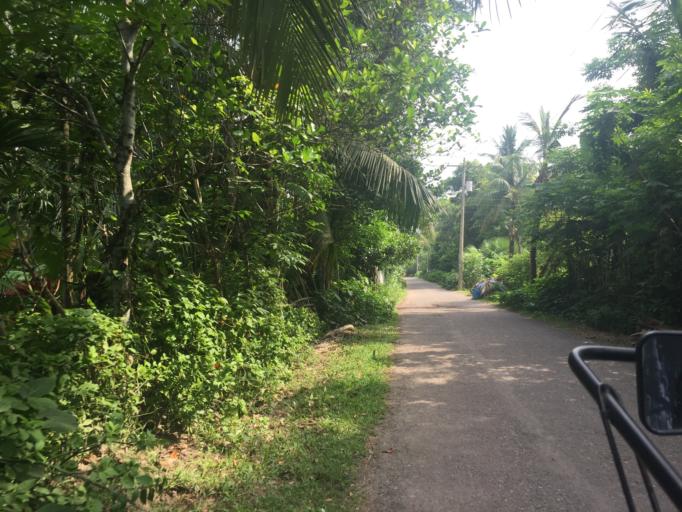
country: BD
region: Barisal
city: Mathba
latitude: 22.2217
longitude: 89.9161
